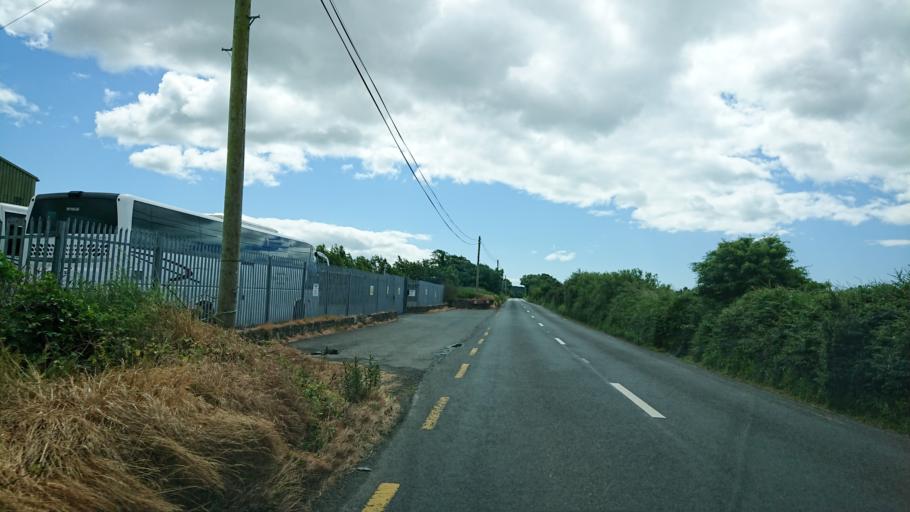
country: IE
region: Munster
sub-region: Waterford
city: Tra Mhor
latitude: 52.1936
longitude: -7.1868
